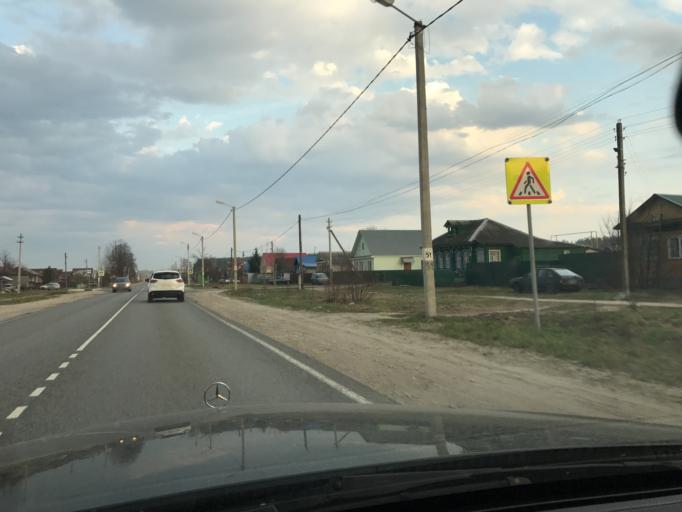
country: RU
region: Vladimir
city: Murom
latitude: 55.6063
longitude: 41.9611
